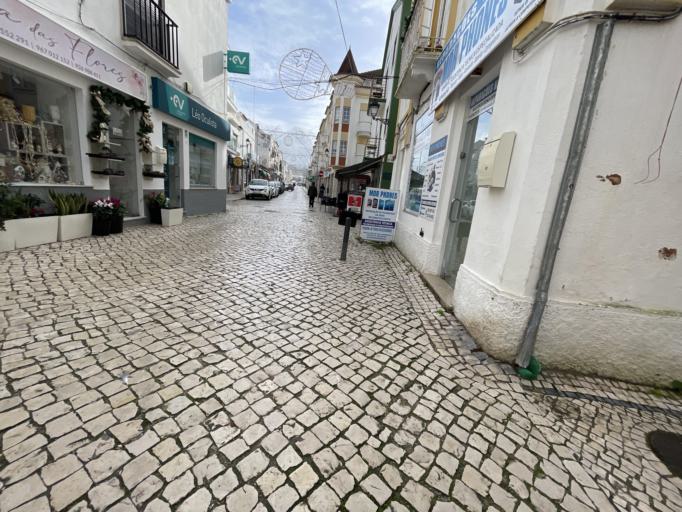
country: PT
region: Leiria
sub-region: Nazare
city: Nazare
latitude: 39.6002
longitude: -9.0709
